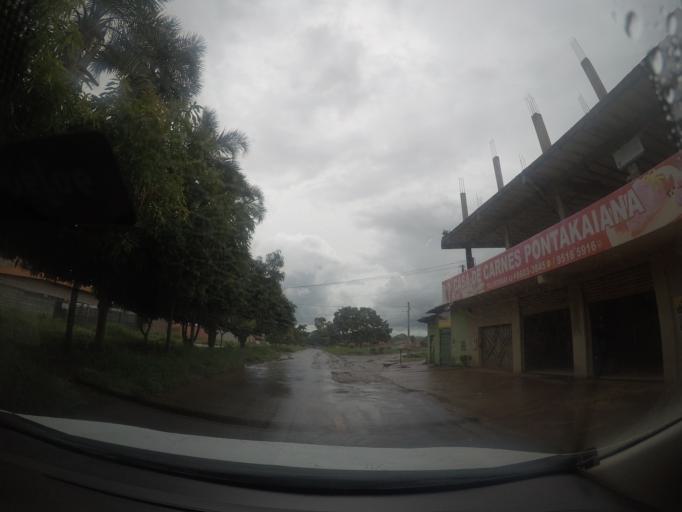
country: BR
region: Goias
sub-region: Trindade
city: Trindade
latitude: -16.6396
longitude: -49.4334
